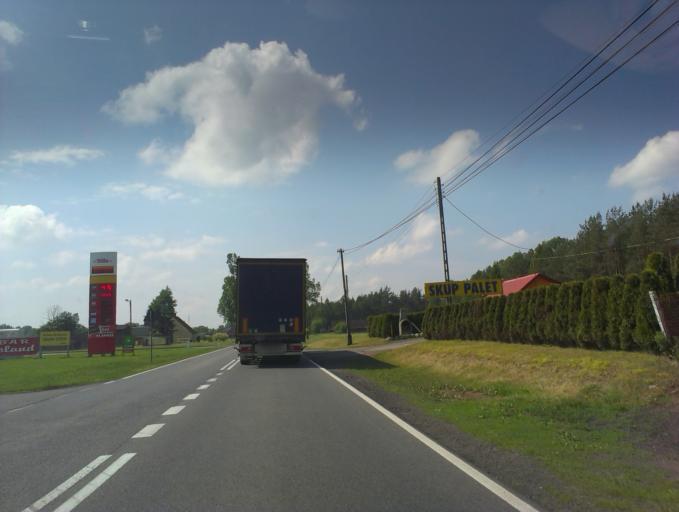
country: PL
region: Greater Poland Voivodeship
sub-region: Powiat zlotowski
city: Jastrowie
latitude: 53.3780
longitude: 16.7939
